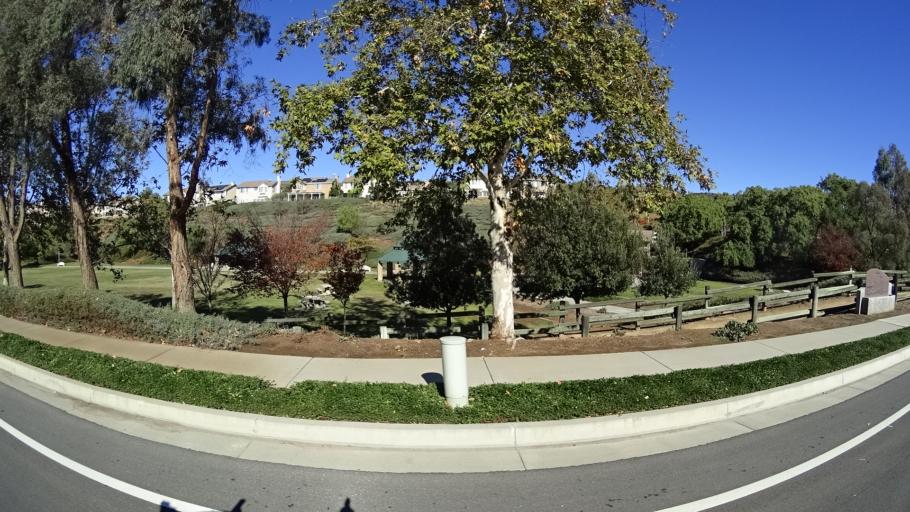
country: US
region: California
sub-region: Orange County
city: Yorba Linda
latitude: 33.9232
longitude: -117.8400
